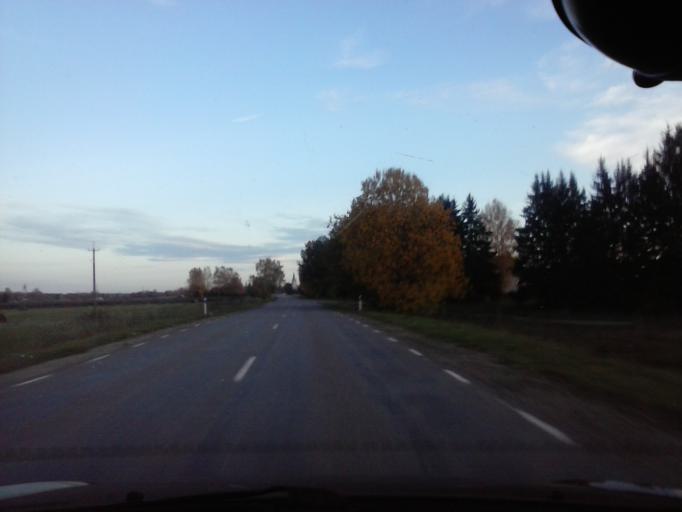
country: EE
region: Raplamaa
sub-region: Maerjamaa vald
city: Marjamaa
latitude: 58.9206
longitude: 24.4114
